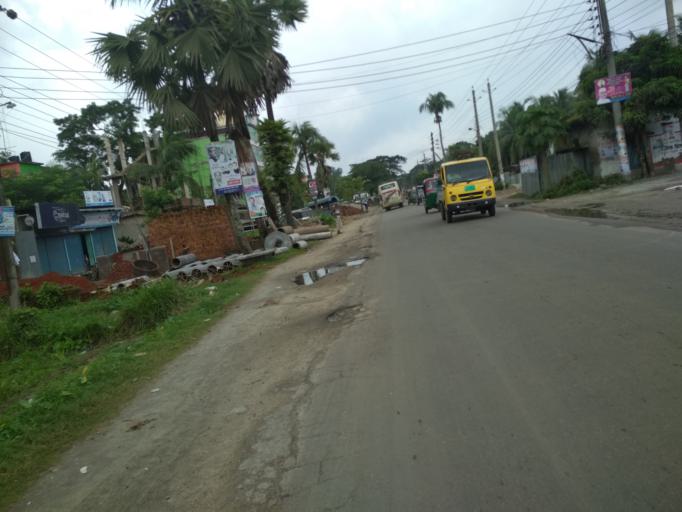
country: BD
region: Chittagong
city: Lakshmipur
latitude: 22.9452
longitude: 90.8242
